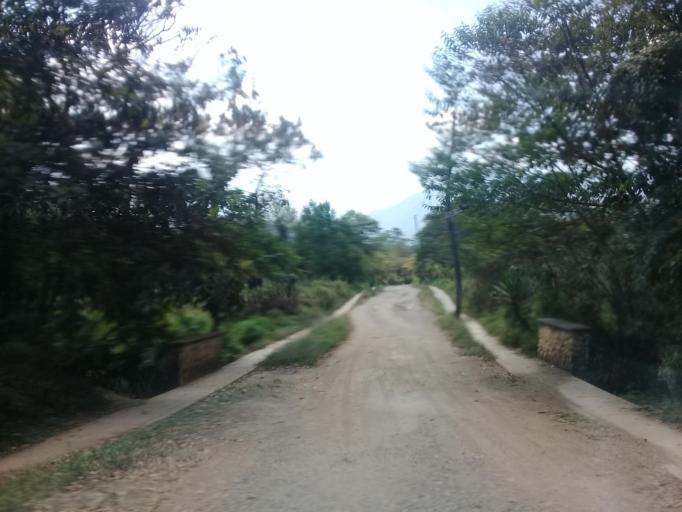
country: MX
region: Veracruz
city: Jalapilla
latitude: 18.8168
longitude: -97.0630
